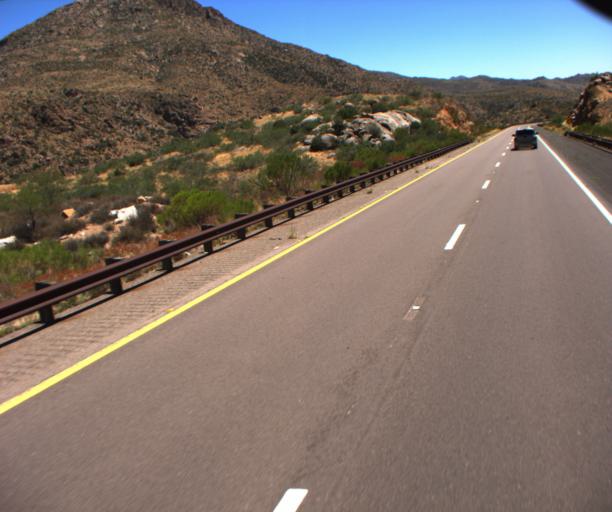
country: US
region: Arizona
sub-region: Gila County
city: Tonto Basin
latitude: 33.8447
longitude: -111.4695
